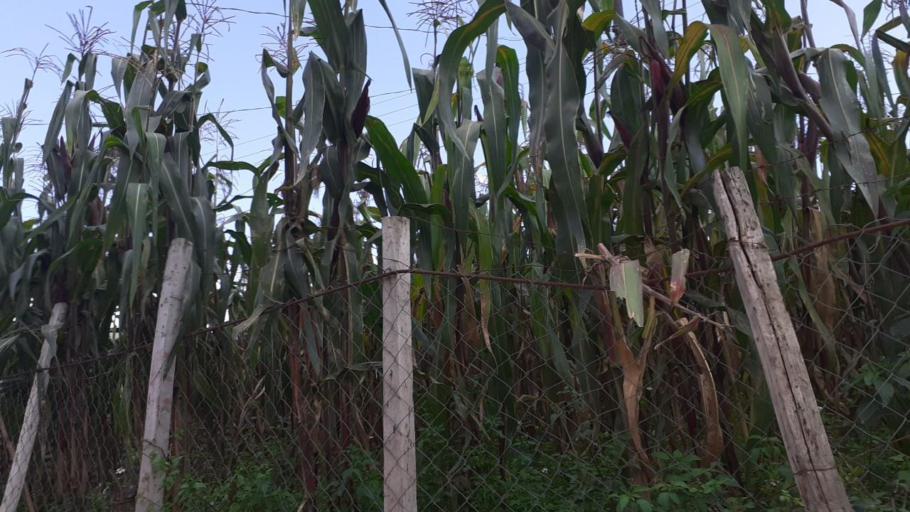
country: GT
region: Quetzaltenango
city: Ostuncalco
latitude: 14.8649
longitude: -91.6269
